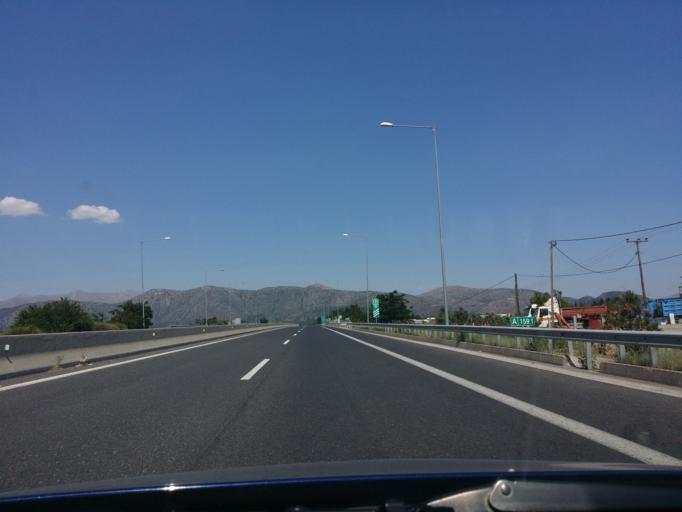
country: GR
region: Peloponnese
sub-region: Nomos Arkadias
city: Tripoli
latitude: 37.4996
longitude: 22.3928
